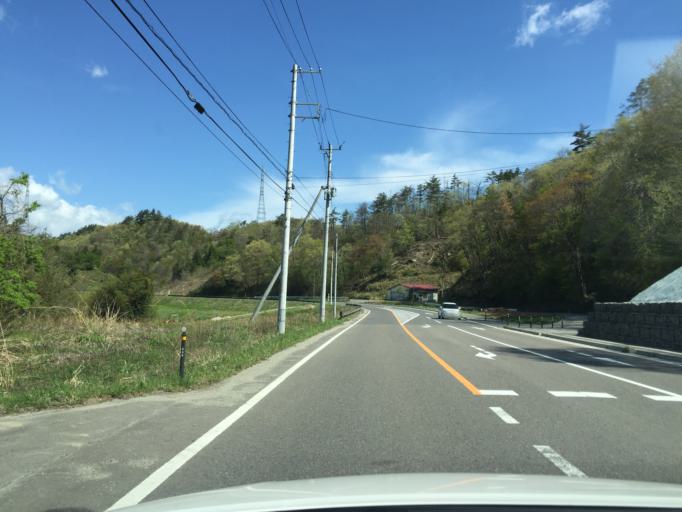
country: JP
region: Fukushima
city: Funehikimachi-funehiki
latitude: 37.5418
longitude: 140.5358
